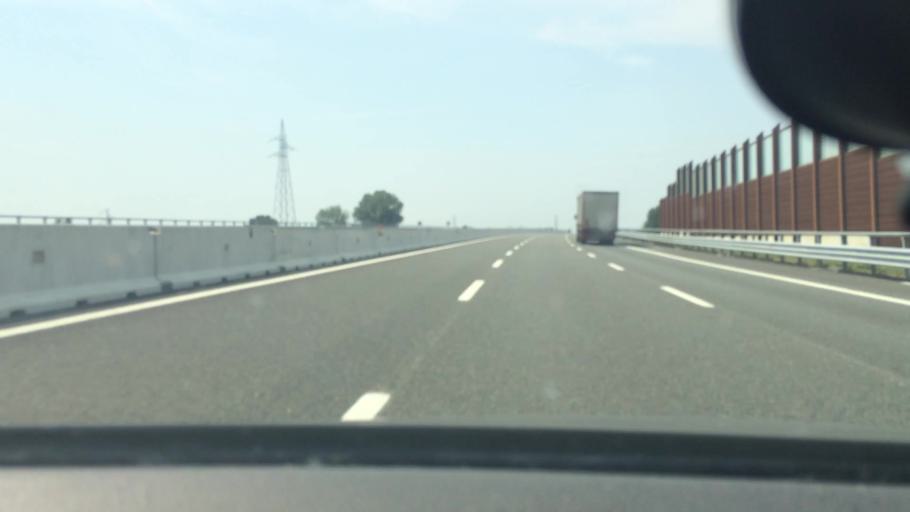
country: IT
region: Lombardy
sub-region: Citta metropolitana di Milano
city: Dresano
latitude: 45.3734
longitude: 9.3732
